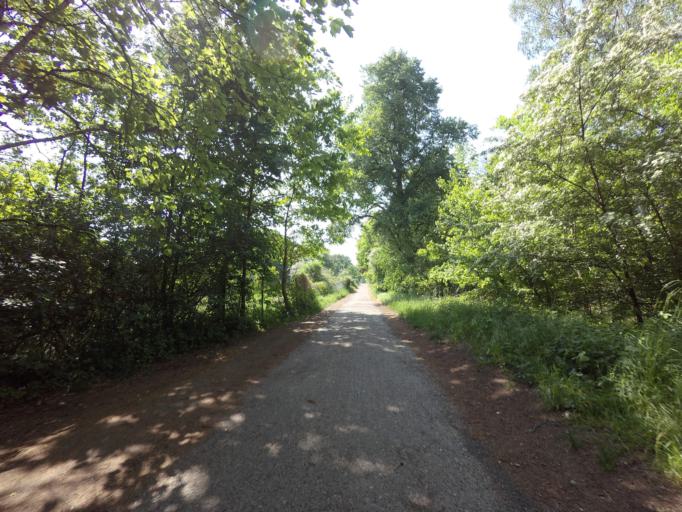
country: DE
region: Lower Saxony
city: Braunschweig
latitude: 52.2931
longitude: 10.5500
